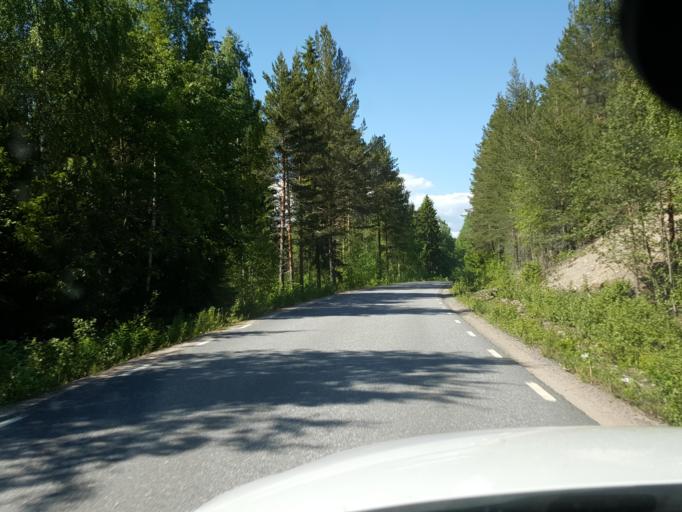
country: SE
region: Gaevleborg
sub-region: Ljusdals Kommun
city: Jaervsoe
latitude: 61.7662
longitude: 16.2159
